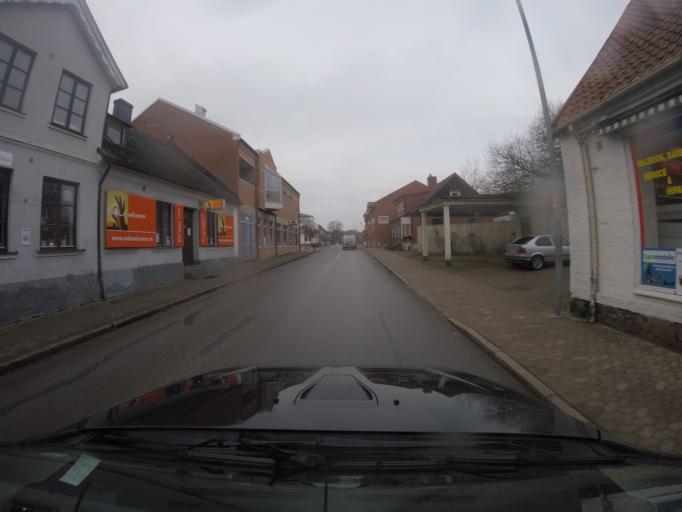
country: SE
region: Skane
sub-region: Svedala Kommun
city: Svedala
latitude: 55.5104
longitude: 13.2391
